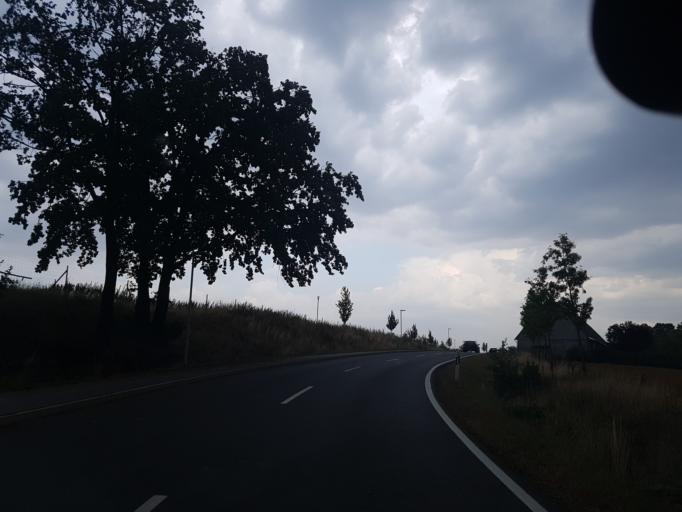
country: DE
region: Saxony
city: Ebersbach
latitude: 51.0921
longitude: 13.0927
